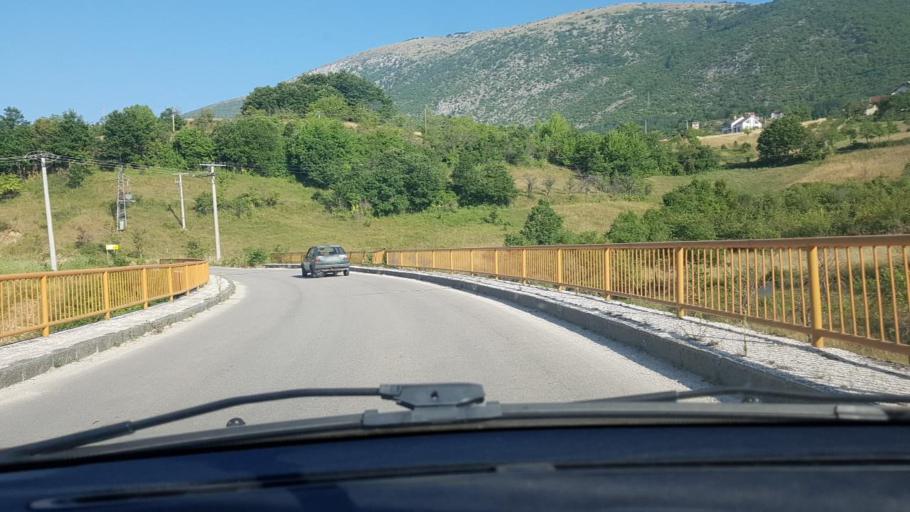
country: BA
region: Federation of Bosnia and Herzegovina
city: Rumboci
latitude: 43.8289
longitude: 17.5222
